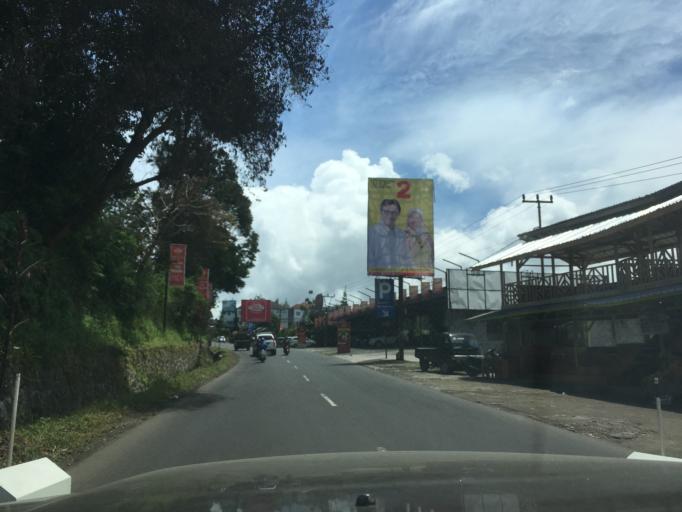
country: ID
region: West Java
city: Lembang
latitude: -6.8039
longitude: 107.6494
